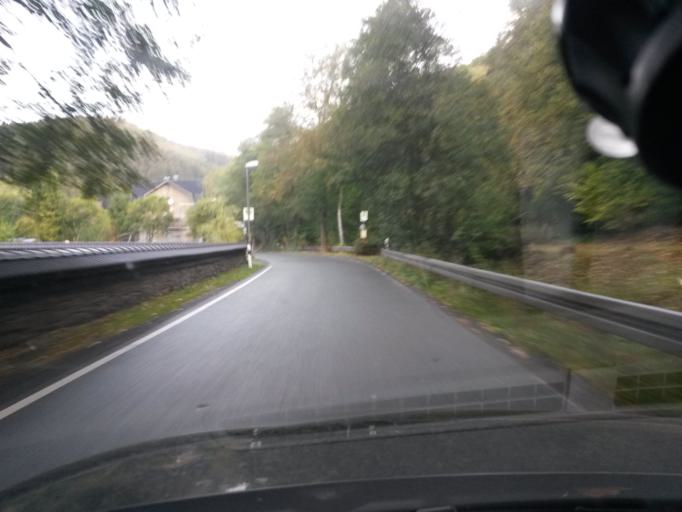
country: DE
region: North Rhine-Westphalia
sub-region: Regierungsbezirk Arnsberg
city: Herscheid
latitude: 51.2183
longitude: 7.7247
